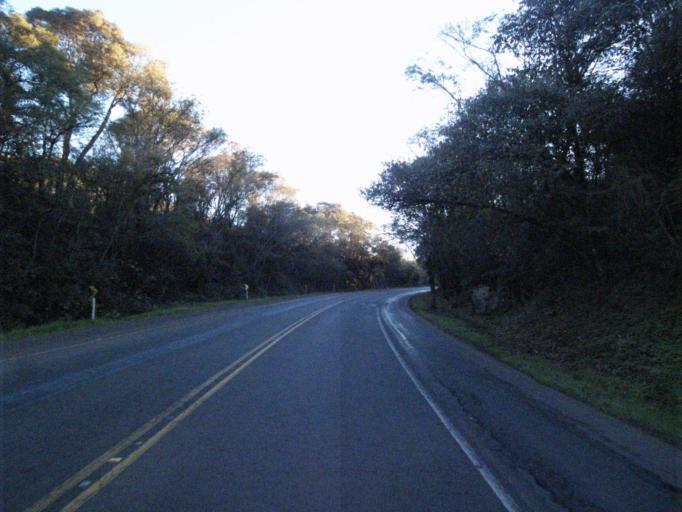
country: BR
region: Santa Catarina
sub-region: Sao Lourenco Do Oeste
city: Sao Lourenco dOeste
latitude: -26.8291
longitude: -53.1104
